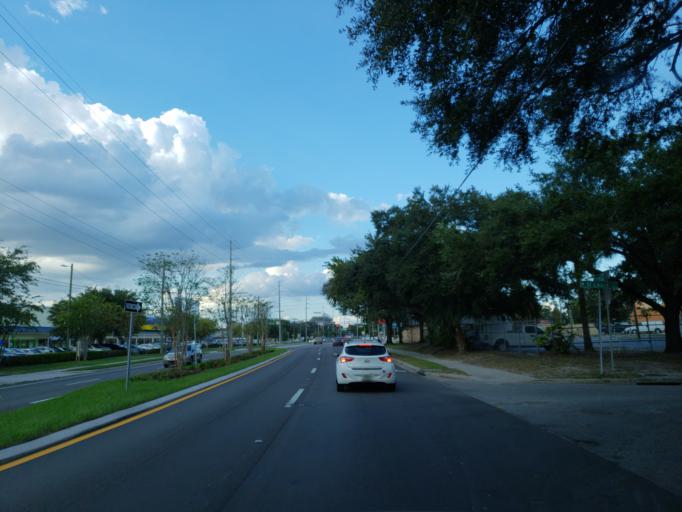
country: US
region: Florida
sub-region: Hillsborough County
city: Tampa
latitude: 27.9653
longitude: -82.5014
